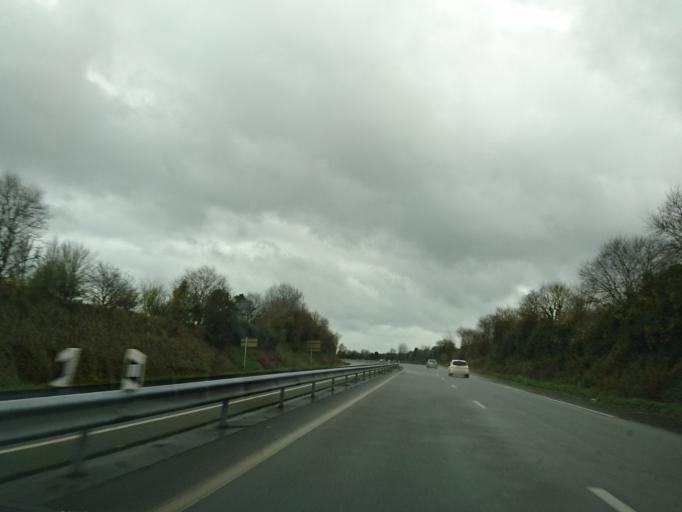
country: FR
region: Brittany
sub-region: Departement du Finistere
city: Guilers
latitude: 48.3946
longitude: -4.5416
